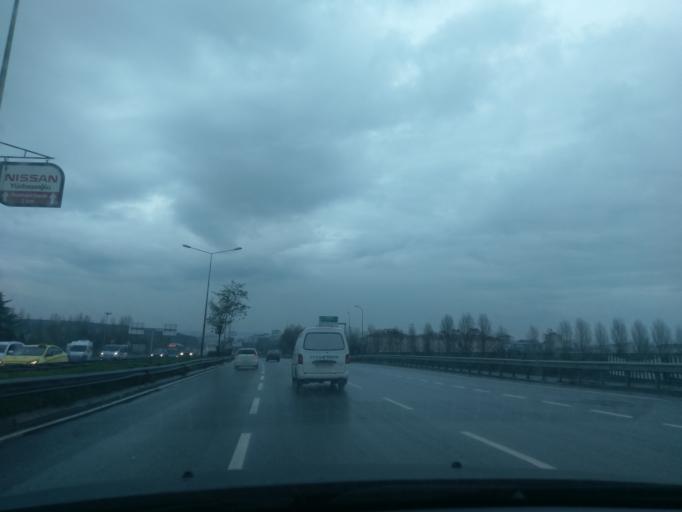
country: TR
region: Istanbul
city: Samandira
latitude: 41.0157
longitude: 29.2048
